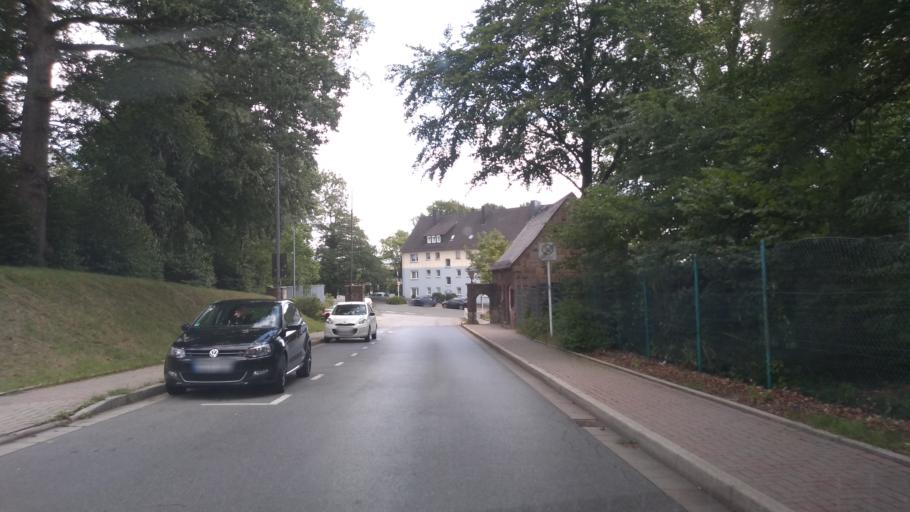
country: DE
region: North Rhine-Westphalia
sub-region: Regierungsbezirk Arnsberg
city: Luedenscheid
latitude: 51.2259
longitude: 7.6046
